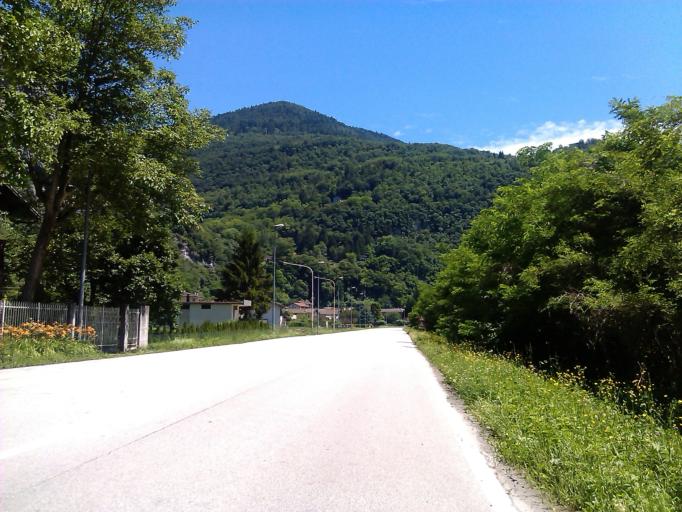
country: IT
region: Veneto
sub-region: Provincia di Vicenza
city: Enego
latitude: 45.9652
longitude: 11.7039
